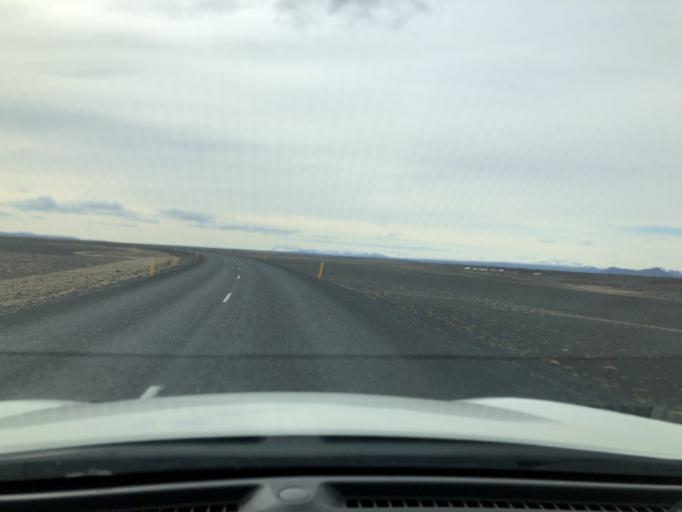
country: IS
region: Northeast
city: Laugar
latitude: 65.6836
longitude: -16.3843
